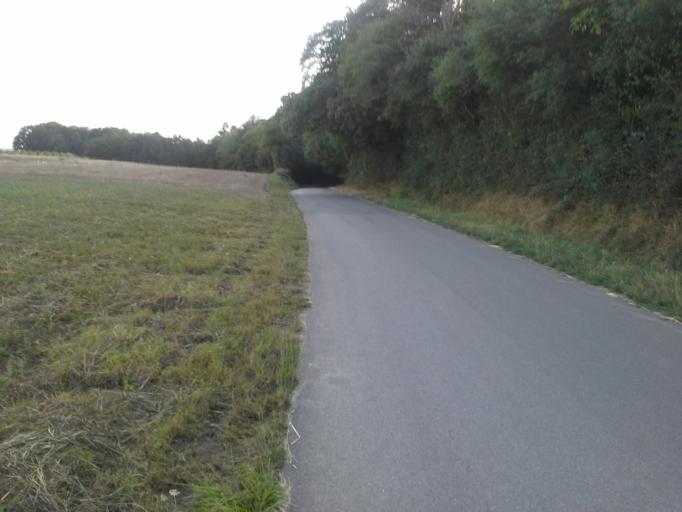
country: FR
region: Centre
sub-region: Departement du Loir-et-Cher
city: Villiers-sur-Loir
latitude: 47.8161
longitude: 0.9882
